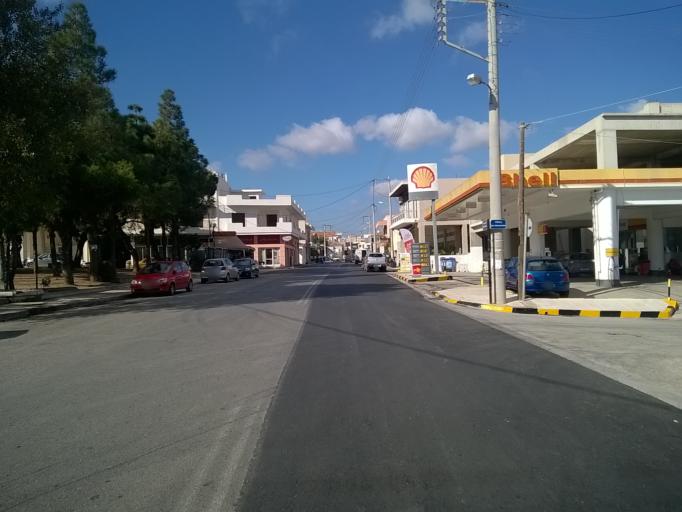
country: GR
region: Attica
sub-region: Nomarchia Anatolikis Attikis
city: Keratea
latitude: 37.8062
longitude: 23.9832
